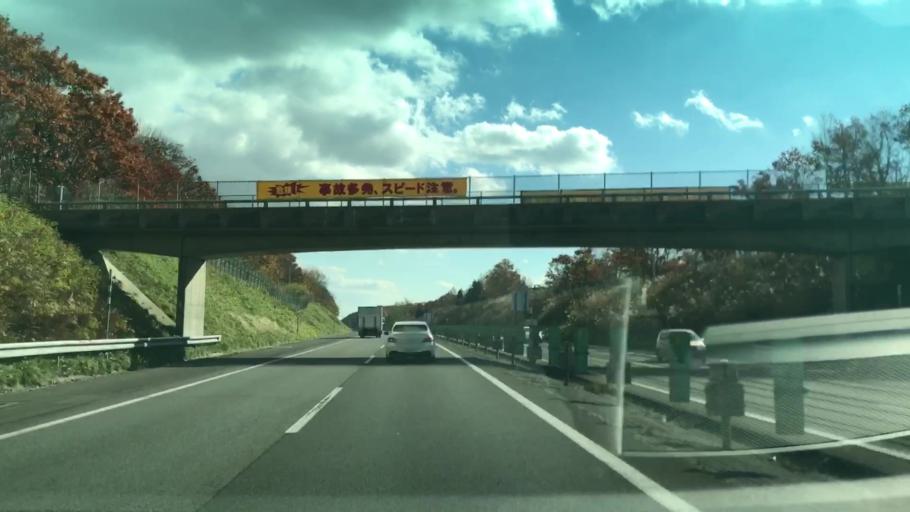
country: JP
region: Hokkaido
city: Kitahiroshima
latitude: 42.9373
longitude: 141.5243
